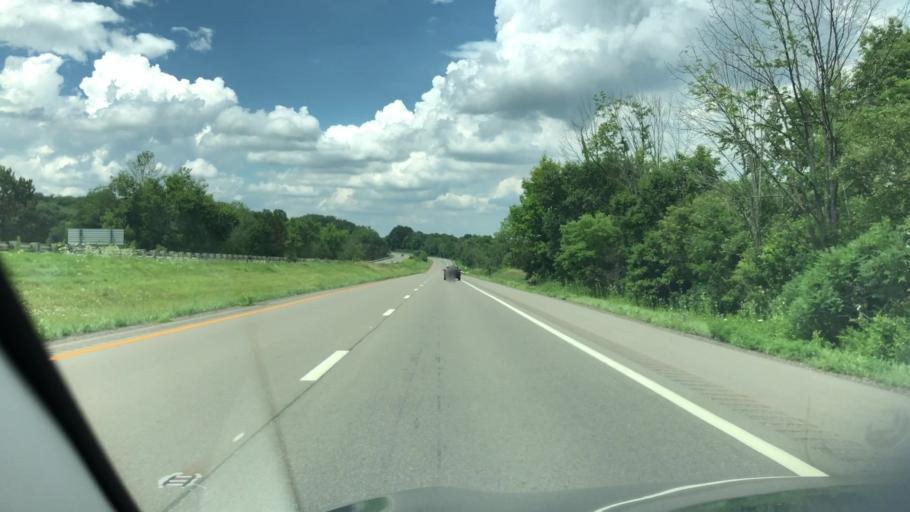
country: US
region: Ohio
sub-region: Stark County
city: Massillon
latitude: 40.8429
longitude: -81.5553
